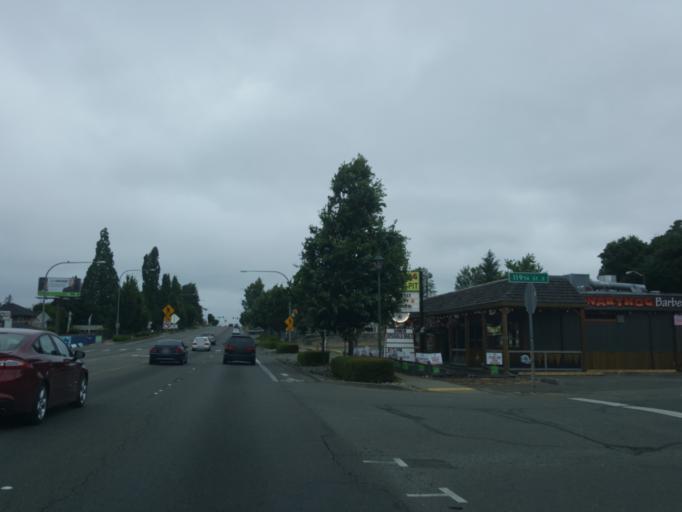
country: US
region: Washington
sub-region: Pierce County
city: Parkland
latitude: 47.1486
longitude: -122.4343
